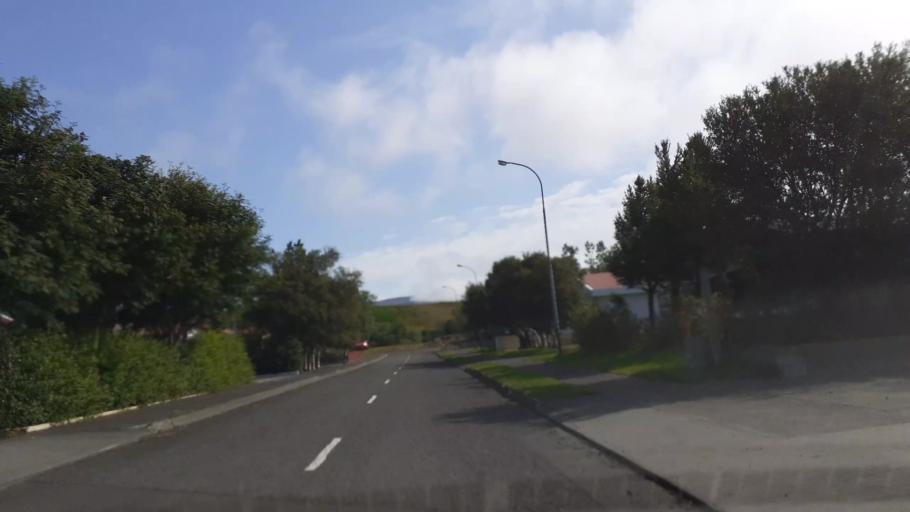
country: IS
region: Northwest
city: Saudarkrokur
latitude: 65.6622
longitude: -20.2757
